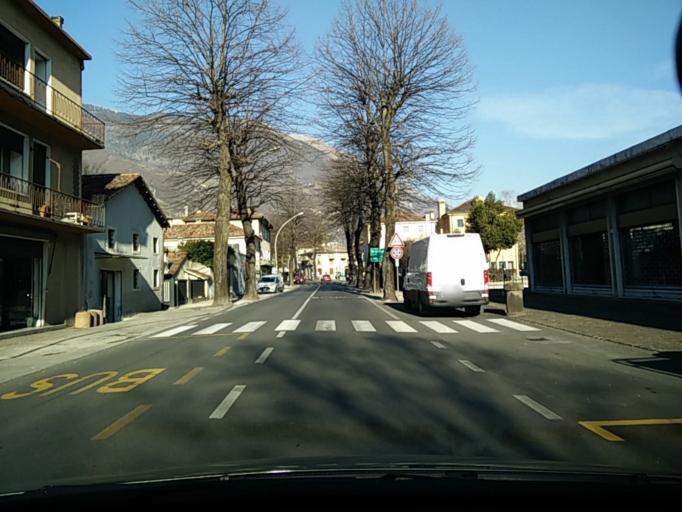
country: IT
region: Veneto
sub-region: Provincia di Treviso
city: Revine
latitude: 46.0044
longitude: 12.2861
